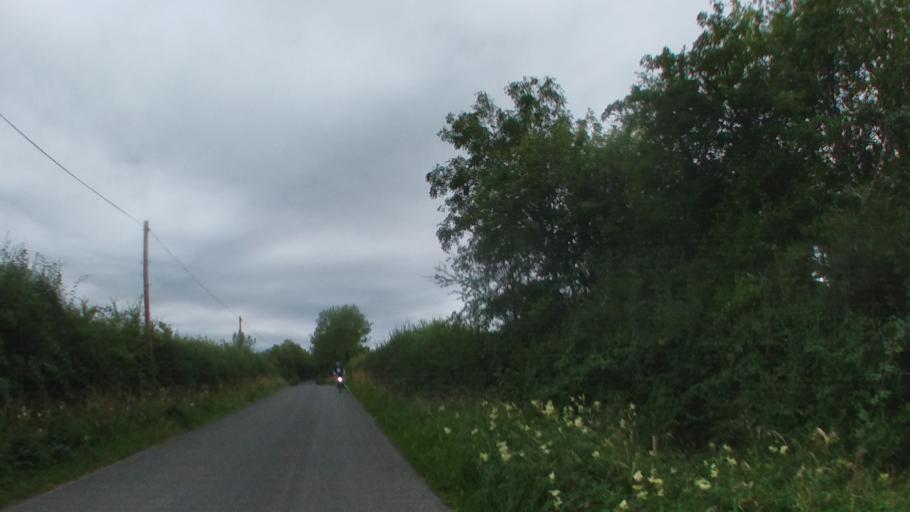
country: IE
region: Leinster
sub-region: Kilkenny
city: Kilkenny
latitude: 52.6820
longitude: -7.2209
